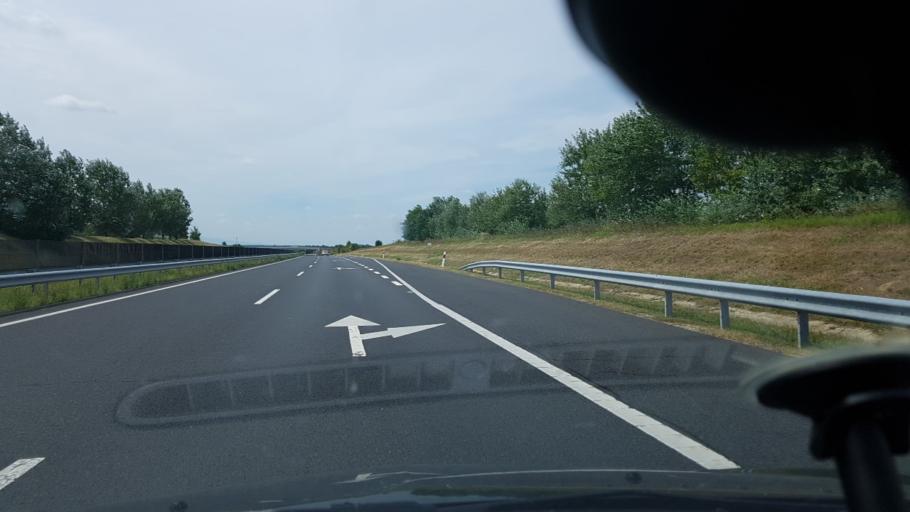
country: HU
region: Zala
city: Becsehely
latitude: 46.4471
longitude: 16.8266
